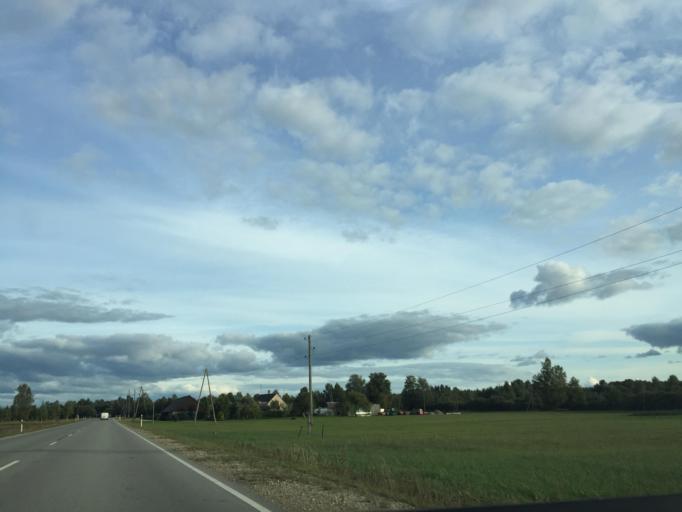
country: LV
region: Jaunjelgava
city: Jaunjelgava
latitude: 56.3770
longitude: 24.9932
